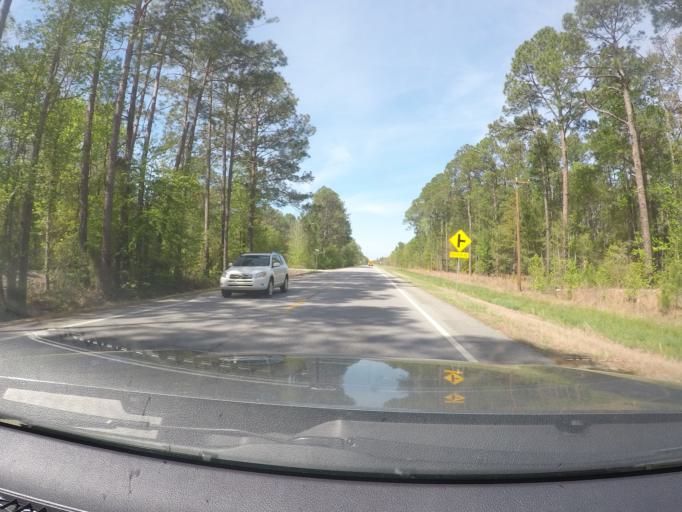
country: US
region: Georgia
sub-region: Bryan County
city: Pembroke
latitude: 32.1321
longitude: -81.5699
